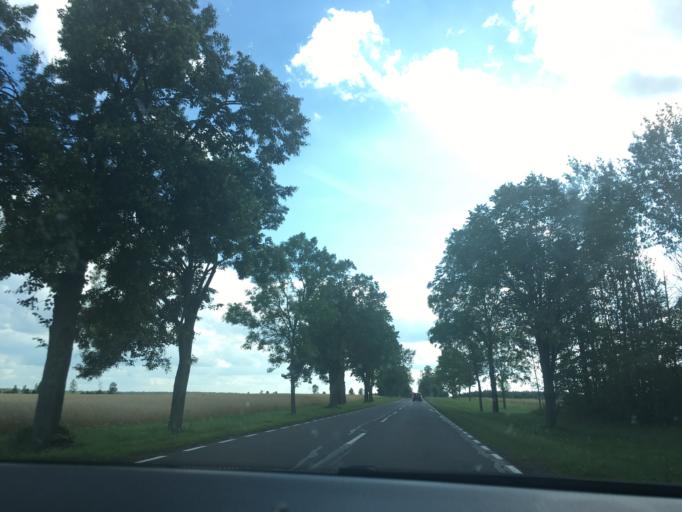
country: PL
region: Podlasie
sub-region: Powiat bielski
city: Bielsk Podlaski
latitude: 52.8894
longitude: 23.2184
